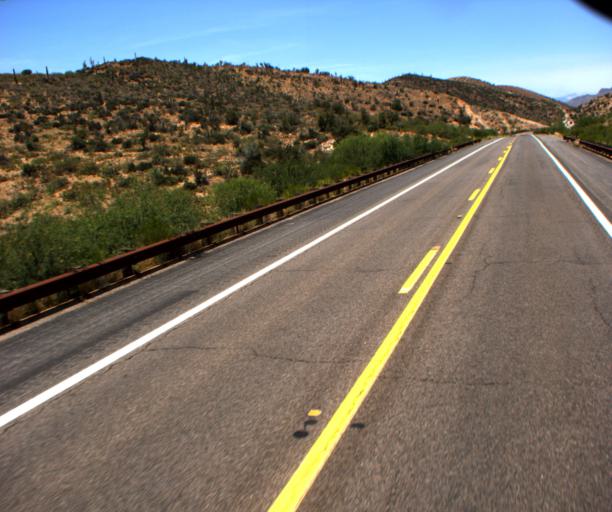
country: US
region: Arizona
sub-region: Gila County
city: Claypool
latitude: 33.4989
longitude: -110.8665
